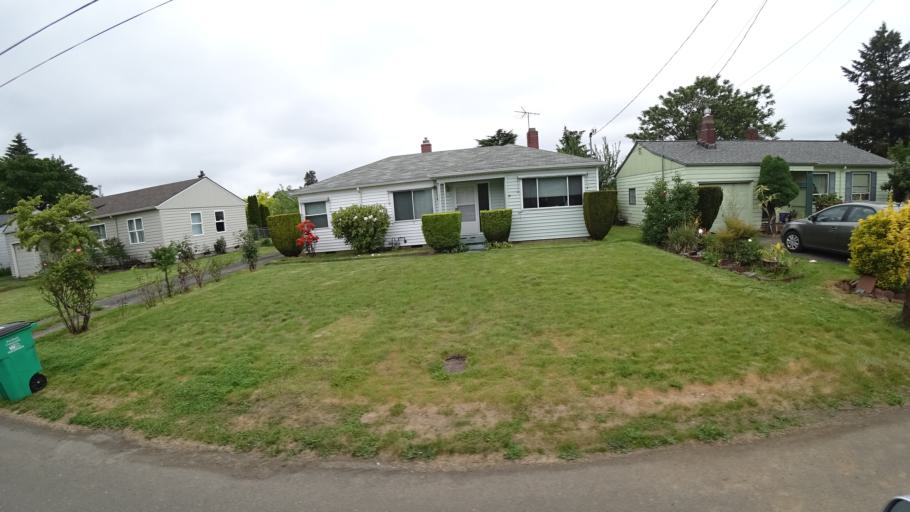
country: US
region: Oregon
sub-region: Multnomah County
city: Portland
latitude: 45.5533
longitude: -122.6110
